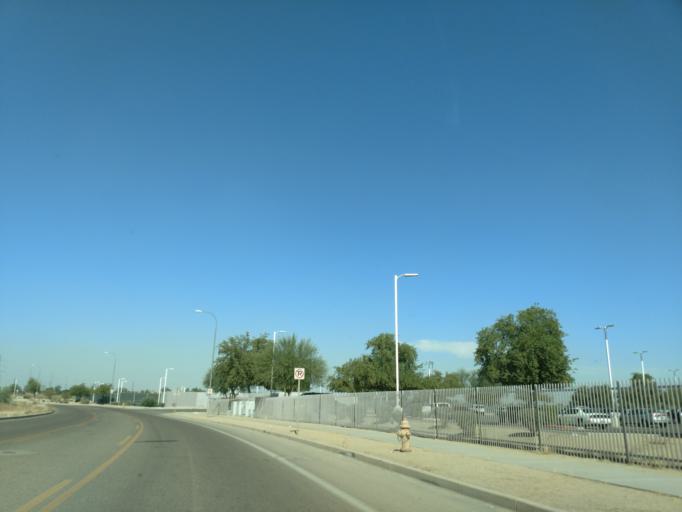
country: US
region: Arizona
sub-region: Maricopa County
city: Laveen
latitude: 33.3721
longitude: -112.1836
